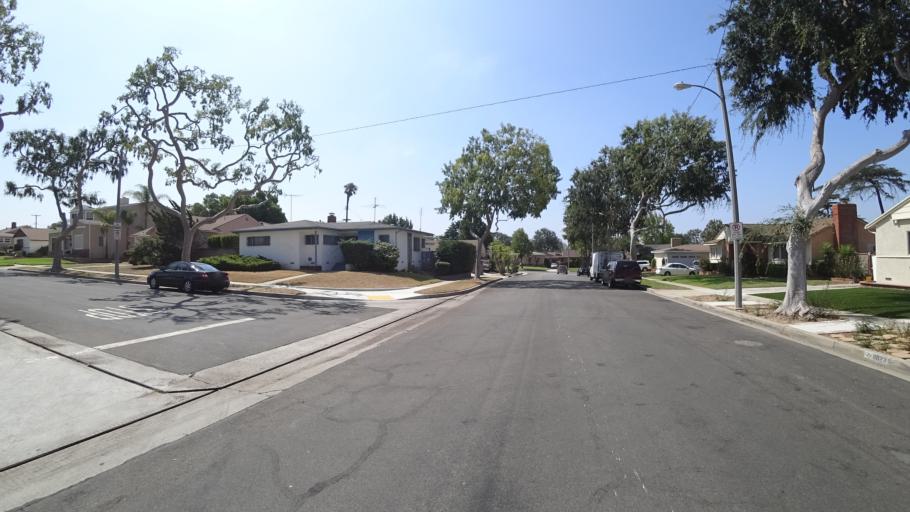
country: US
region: California
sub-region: Los Angeles County
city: Westmont
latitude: 33.9348
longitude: -118.3228
